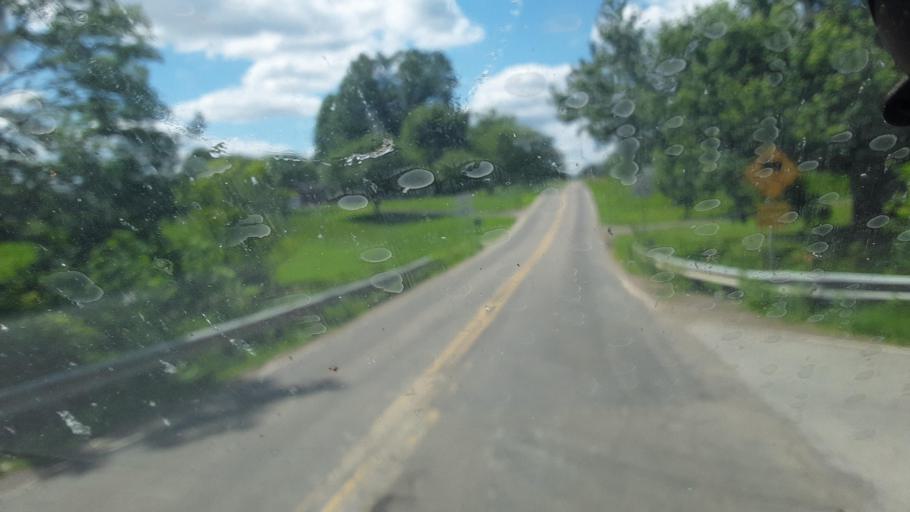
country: US
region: Pennsylvania
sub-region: Lawrence County
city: New Wilmington
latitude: 41.0793
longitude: -80.2651
